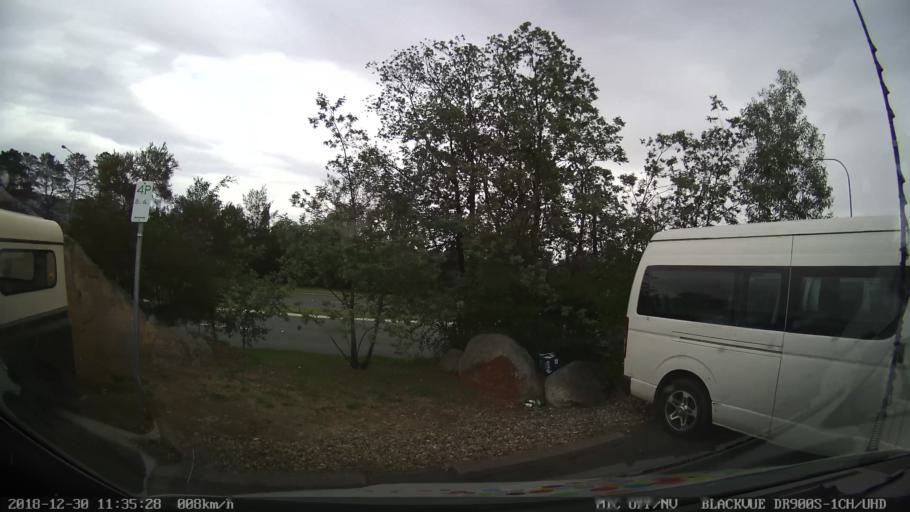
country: AU
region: New South Wales
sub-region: Snowy River
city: Jindabyne
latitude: -36.4144
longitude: 148.6210
